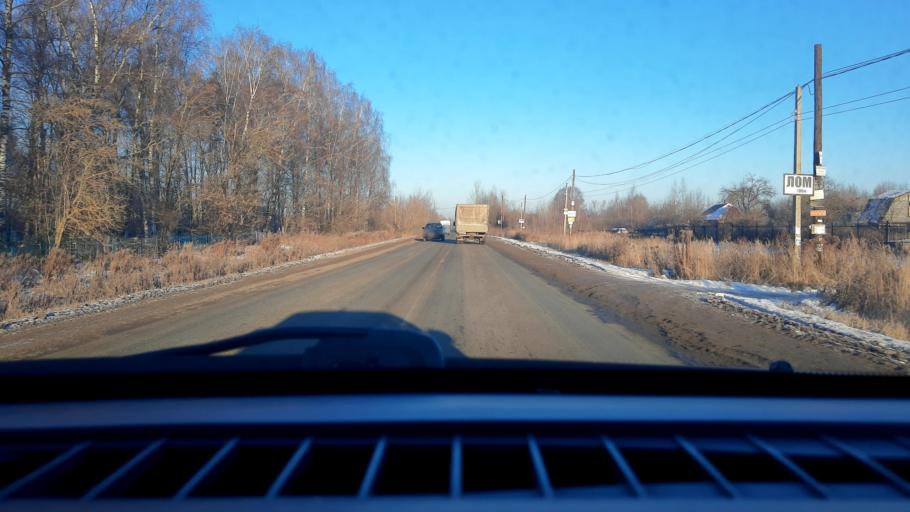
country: RU
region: Nizjnij Novgorod
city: Bor
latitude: 56.3685
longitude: 44.0852
